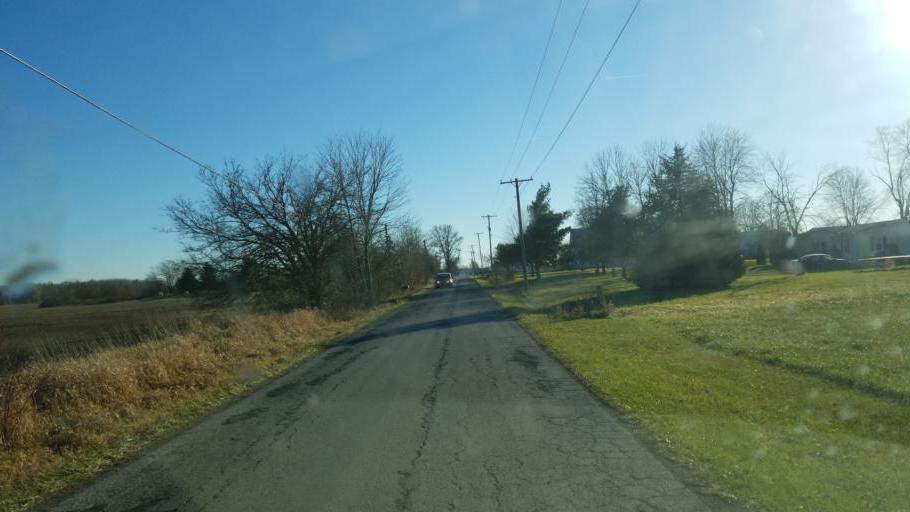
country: US
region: Ohio
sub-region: Morrow County
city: Cardington
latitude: 40.4782
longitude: -82.8955
